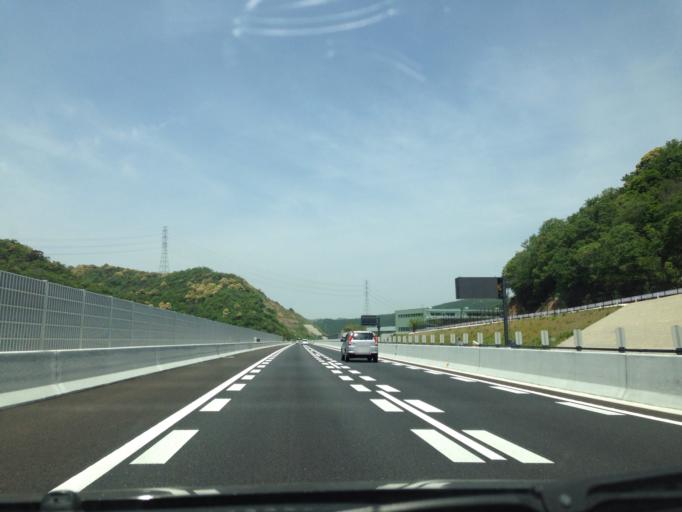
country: JP
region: Aichi
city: Gamagori
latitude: 34.9233
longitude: 137.2721
